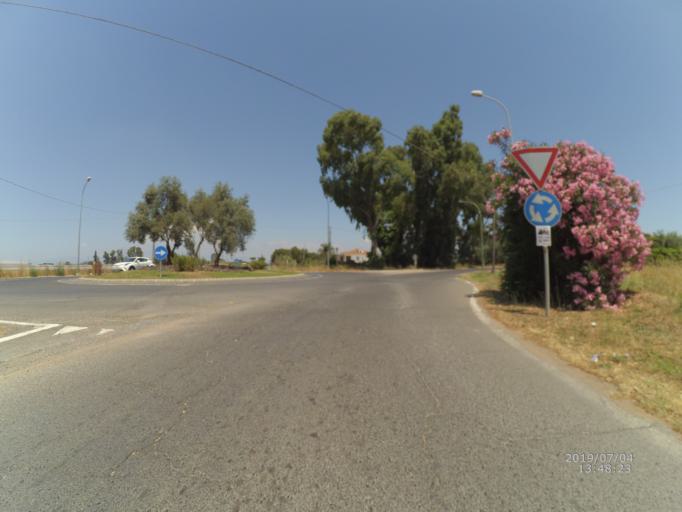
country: IT
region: Latium
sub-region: Provincia di Latina
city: San Felice Circeo
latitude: 41.2847
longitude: 13.1054
